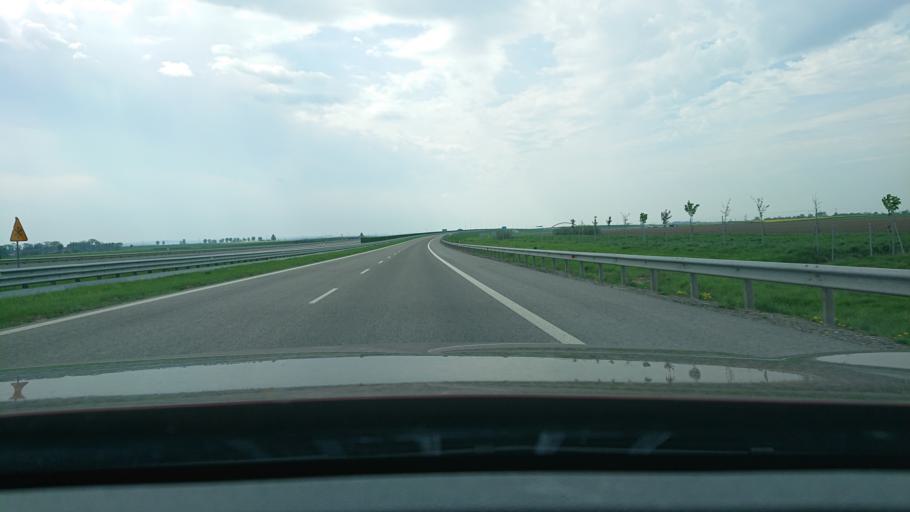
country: PL
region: Subcarpathian Voivodeship
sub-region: Powiat jaroslawski
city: Radymno
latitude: 49.9113
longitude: 22.8328
